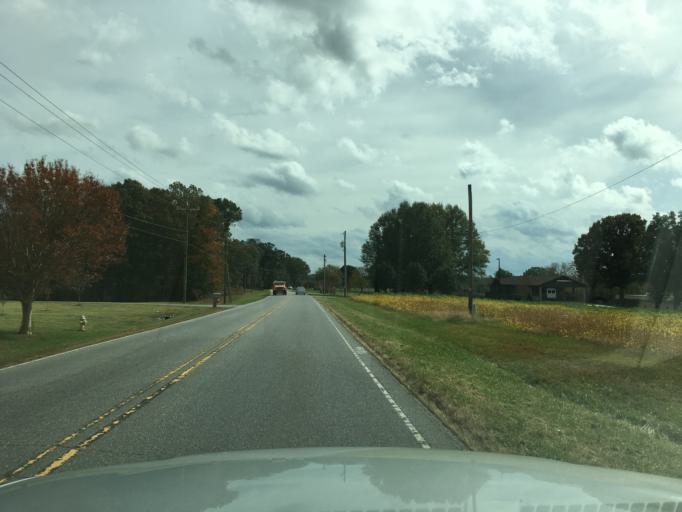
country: US
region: North Carolina
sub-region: Catawba County
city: Newton
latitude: 35.6907
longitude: -81.2825
